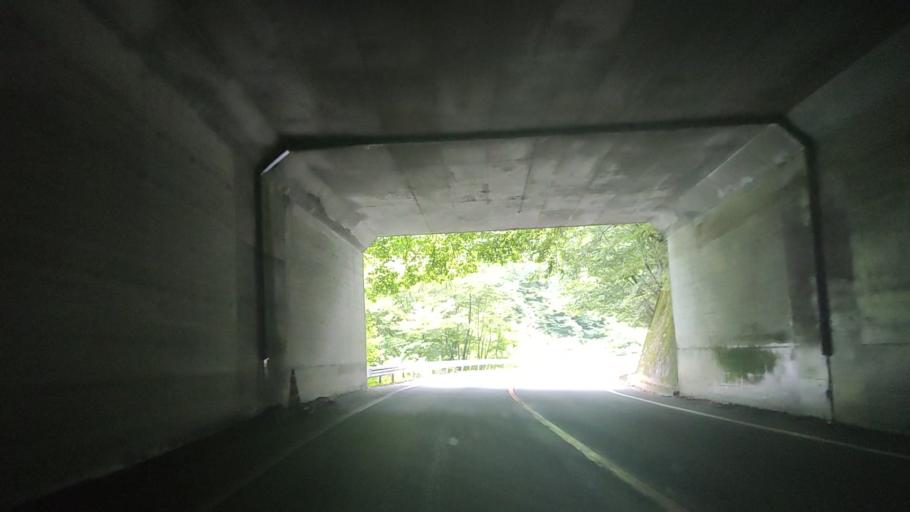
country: JP
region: Tochigi
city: Nikko
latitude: 36.7002
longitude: 139.5079
